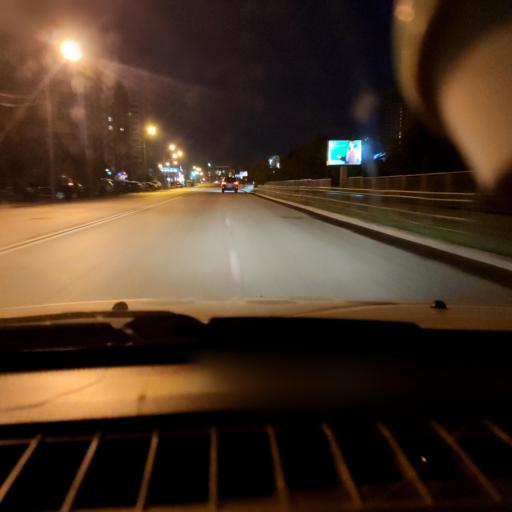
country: RU
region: Sverdlovsk
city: Yekaterinburg
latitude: 56.7960
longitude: 60.6184
